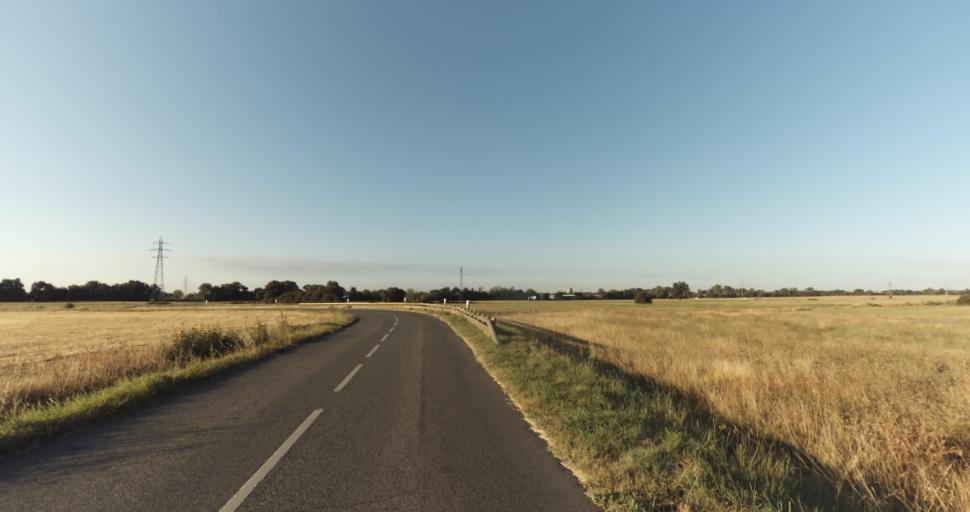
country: FR
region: Midi-Pyrenees
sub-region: Departement de la Haute-Garonne
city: Launaguet
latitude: 43.6691
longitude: 1.4641
